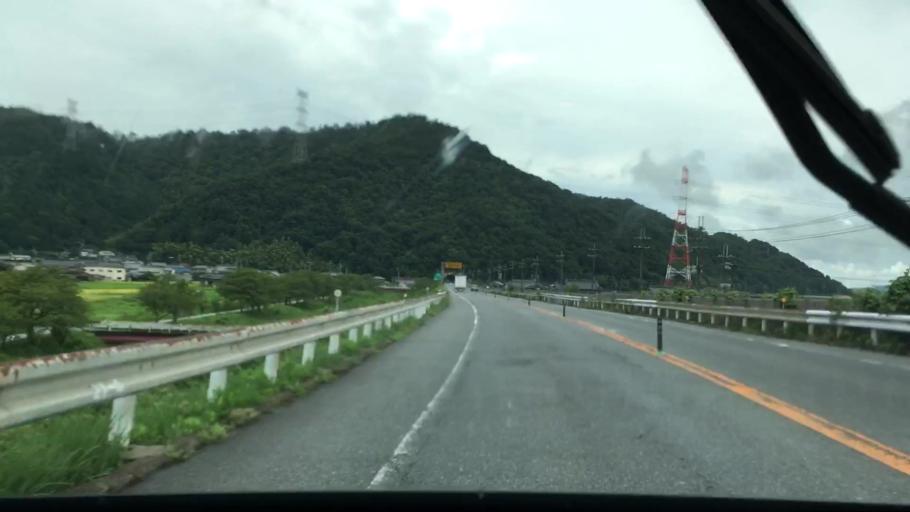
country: JP
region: Hyogo
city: Himeji
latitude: 34.9762
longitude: 134.7687
